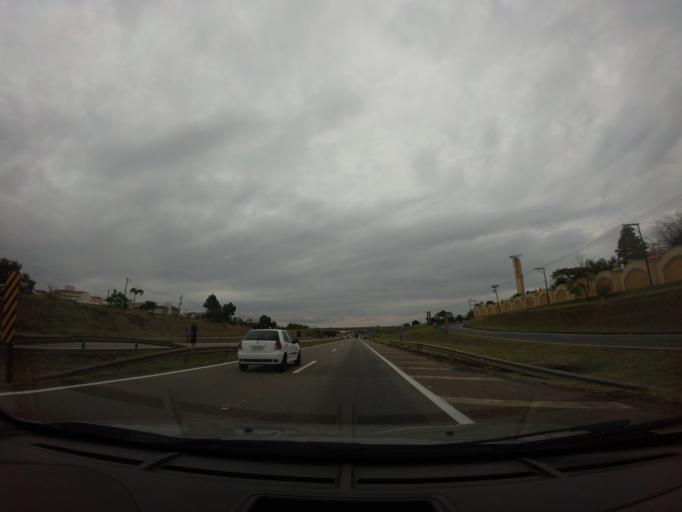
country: BR
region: Sao Paulo
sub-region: Piracicaba
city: Piracicaba
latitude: -22.7382
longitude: -47.6012
